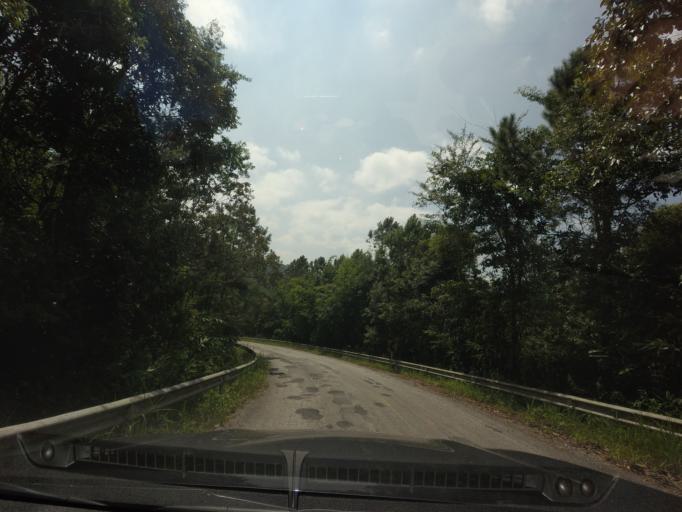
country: TH
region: Loei
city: Na Haeo
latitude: 17.4887
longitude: 100.9392
